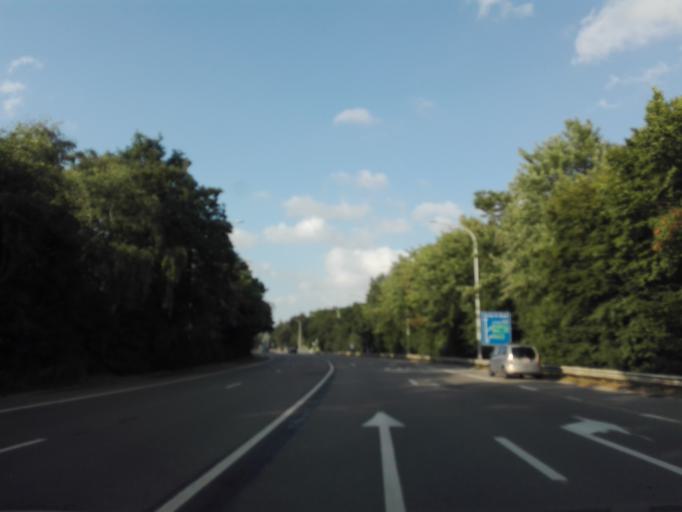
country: BE
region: Wallonia
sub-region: Province du Brabant Wallon
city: Louvain-la-Neuve
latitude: 50.6601
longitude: 4.6458
